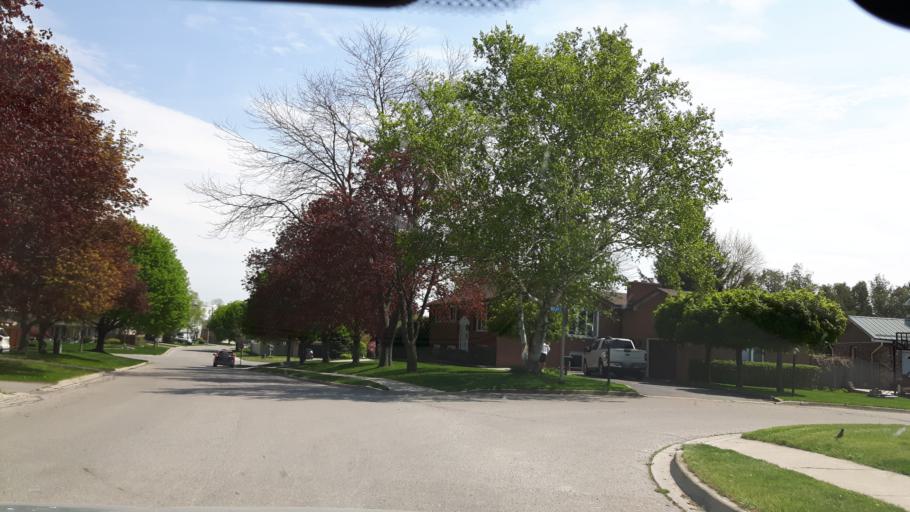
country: CA
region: Ontario
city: Goderich
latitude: 43.7310
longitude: -81.7111
